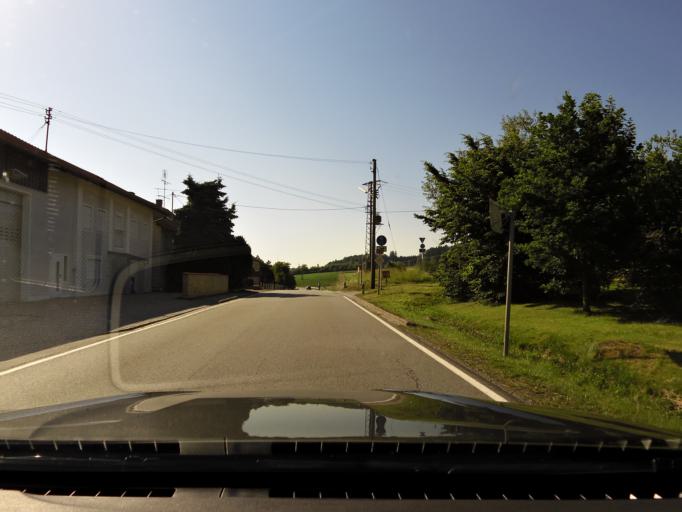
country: DE
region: Bavaria
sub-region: Upper Bavaria
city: Neumarkt-Sankt Veit
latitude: 48.3743
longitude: 12.4790
